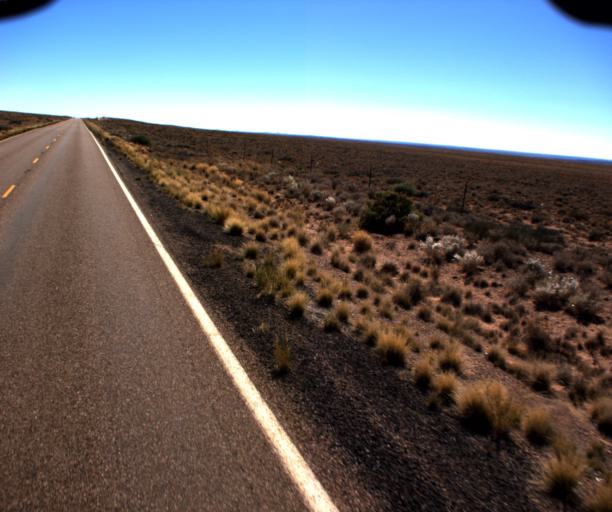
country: US
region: Arizona
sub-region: Navajo County
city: Holbrook
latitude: 35.0189
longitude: -110.0902
